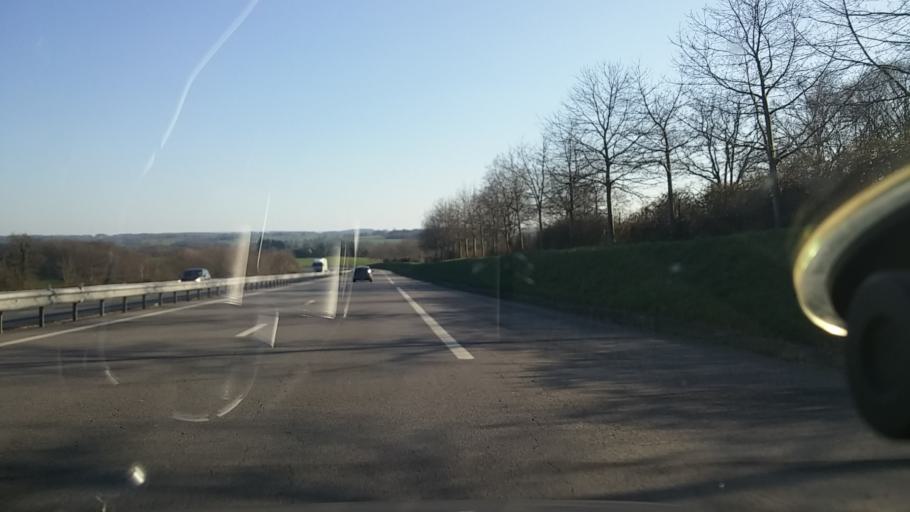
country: FR
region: Limousin
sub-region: Departement de la Haute-Vienne
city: Saint-Sulpice-les-Feuilles
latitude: 46.3023
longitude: 1.4152
